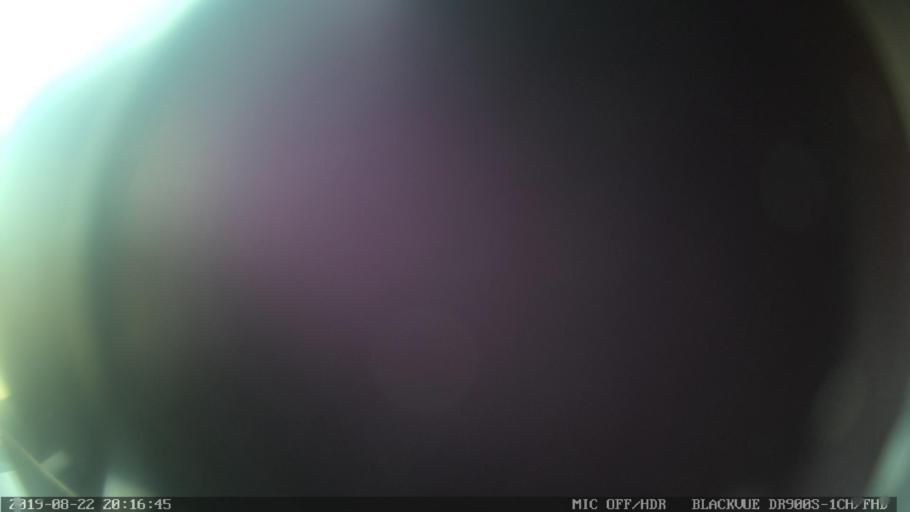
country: PT
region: Guarda
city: Alcains
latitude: 39.9242
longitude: -7.4585
